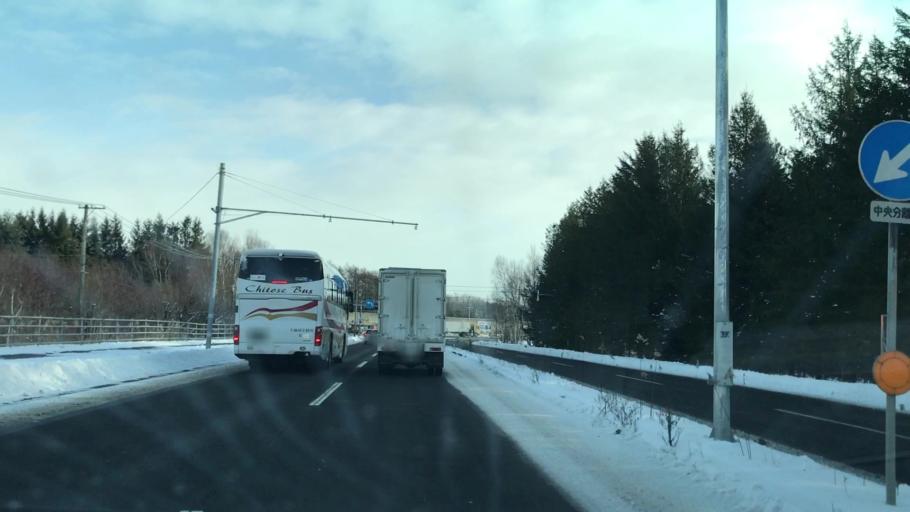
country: JP
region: Hokkaido
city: Chitose
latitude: 42.8183
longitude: 141.6595
